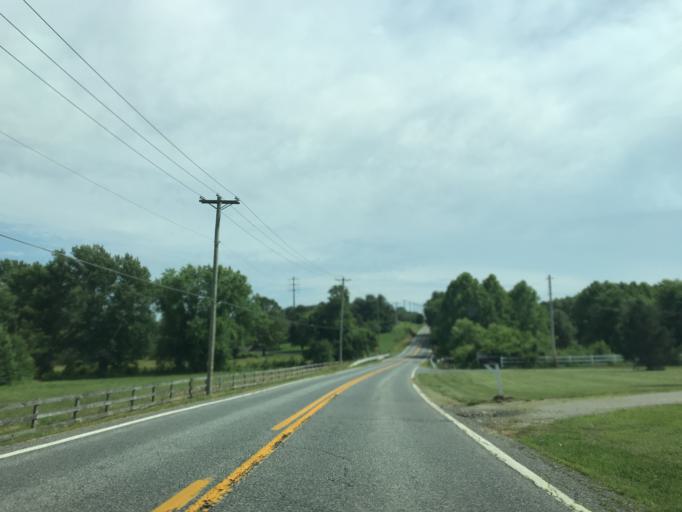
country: US
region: Pennsylvania
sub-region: York County
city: Susquehanna Trails
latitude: 39.6857
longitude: -76.3892
